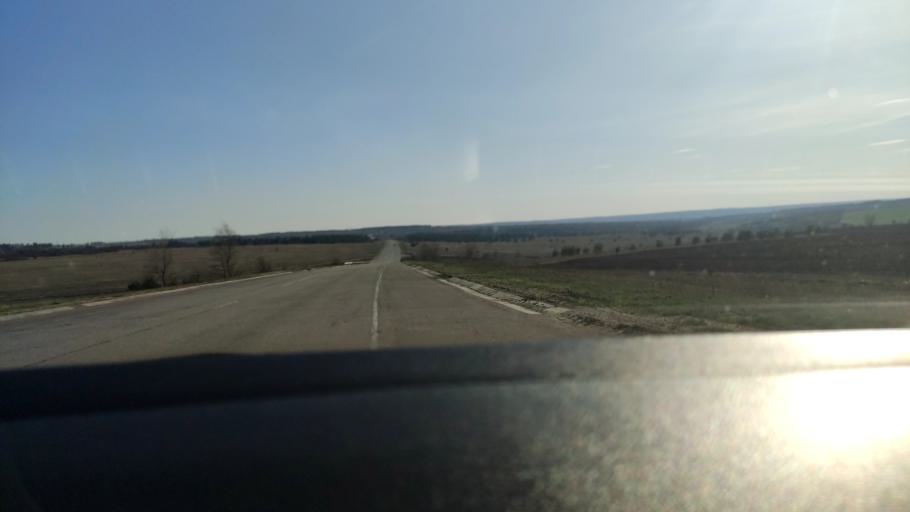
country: RU
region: Voronezj
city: Kolodeznyy
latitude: 51.3903
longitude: 39.2292
